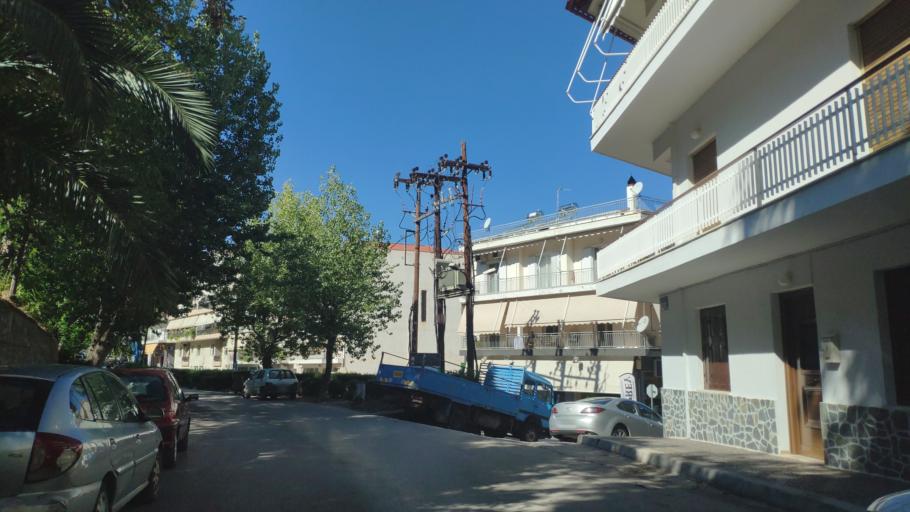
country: GR
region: Central Greece
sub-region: Nomos Voiotias
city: Livadeia
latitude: 38.4388
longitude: 22.8728
